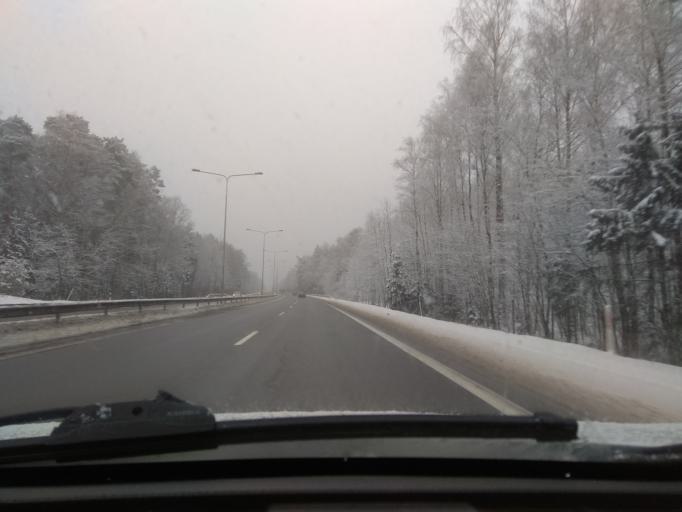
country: LT
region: Kauno apskritis
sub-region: Kauno rajonas
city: Karmelava
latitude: 54.8900
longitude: 24.1662
